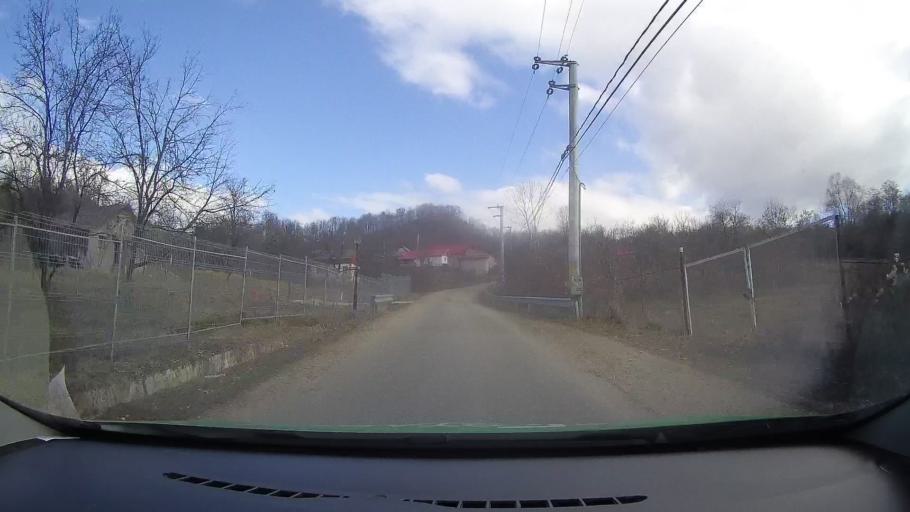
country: RO
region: Dambovita
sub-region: Comuna Varfuri
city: Varfuri
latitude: 45.0991
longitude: 25.5159
